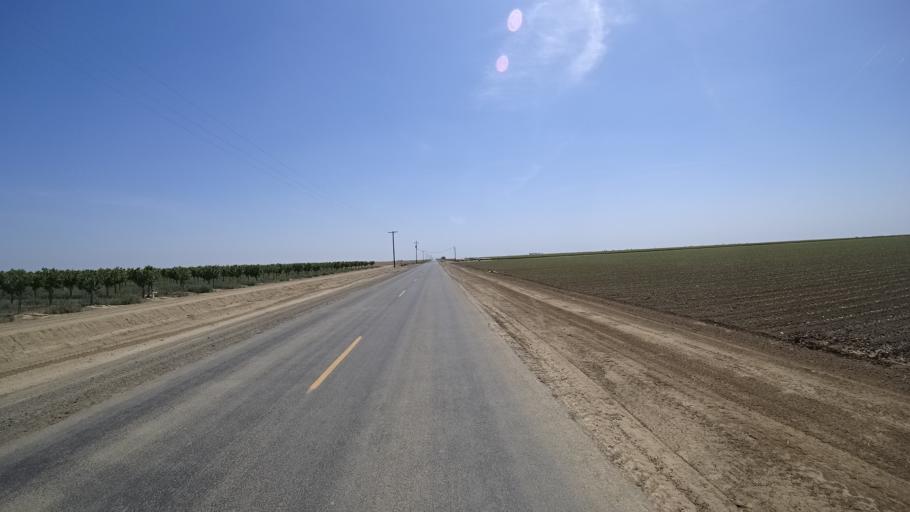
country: US
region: California
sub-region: Kings County
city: Kettleman City
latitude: 36.1377
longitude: -119.9523
